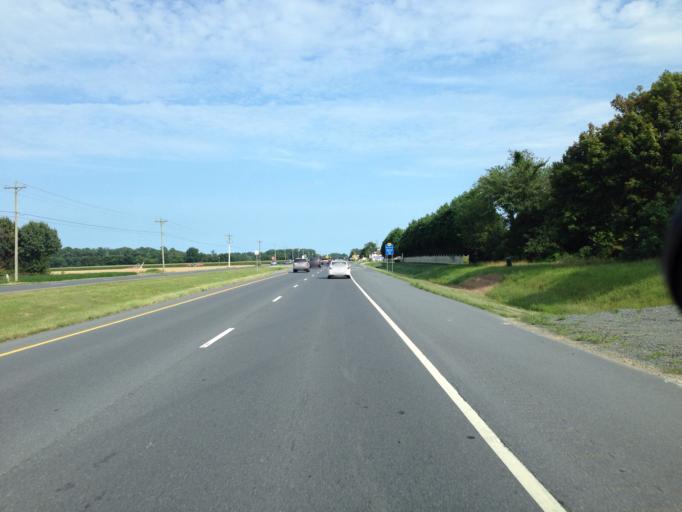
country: US
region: Delaware
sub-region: Sussex County
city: Lewes
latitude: 38.7708
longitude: -75.2195
